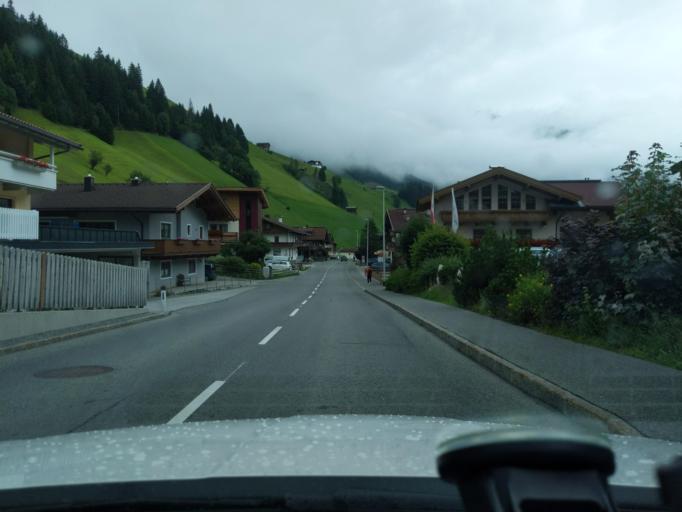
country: AT
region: Tyrol
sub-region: Politischer Bezirk Schwaz
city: Schwendau
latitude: 47.1572
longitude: 11.7293
